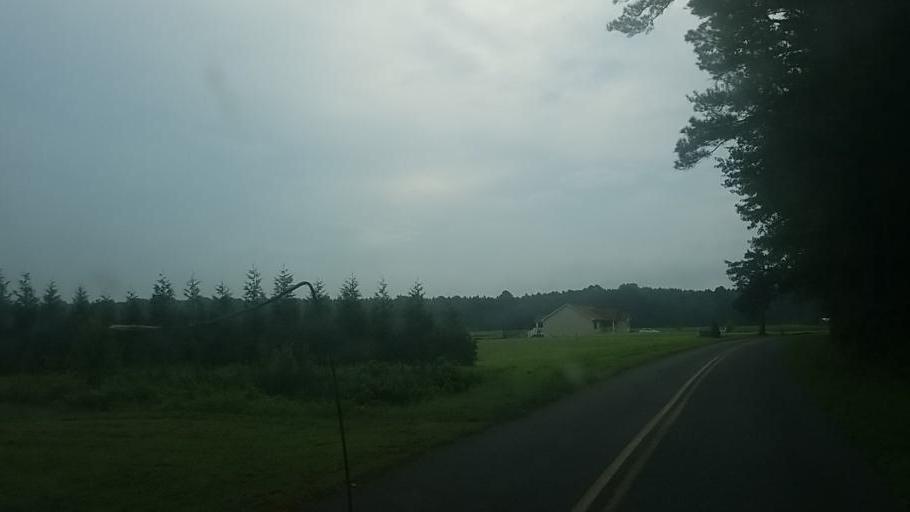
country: US
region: Delaware
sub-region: Sussex County
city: Selbyville
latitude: 38.4261
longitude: -75.2924
